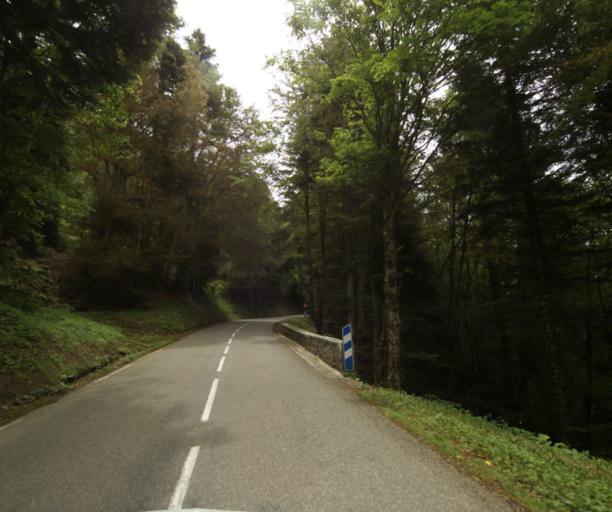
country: FR
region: Rhone-Alpes
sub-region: Departement de la Haute-Savoie
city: Perrignier
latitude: 46.2764
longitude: 6.4551
